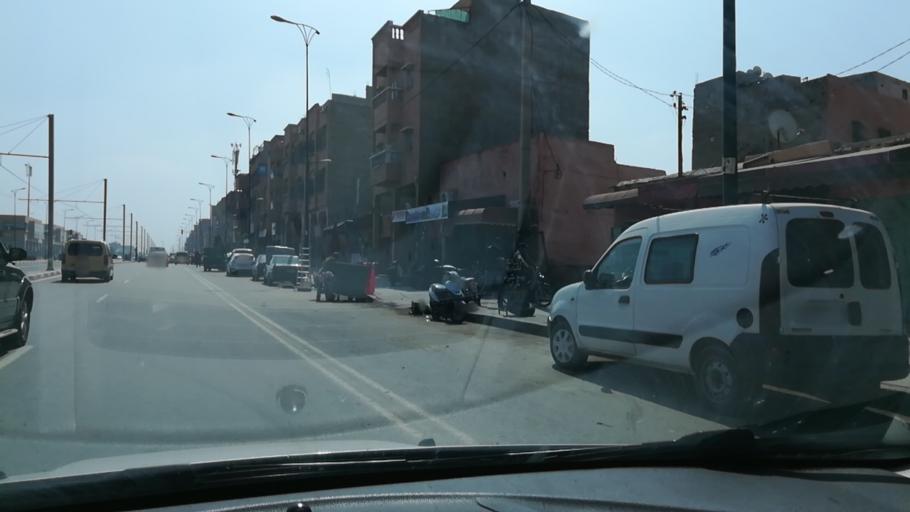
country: MA
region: Marrakech-Tensift-Al Haouz
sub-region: Marrakech
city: Marrakesh
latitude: 31.6278
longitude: -8.0644
